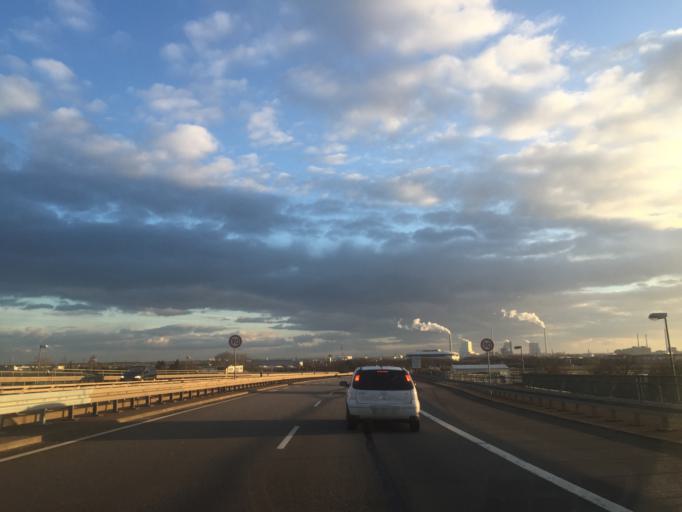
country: DE
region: Baden-Wuerttemberg
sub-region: Karlsruhe Region
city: Ilvesheim
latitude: 49.4781
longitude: 8.5243
